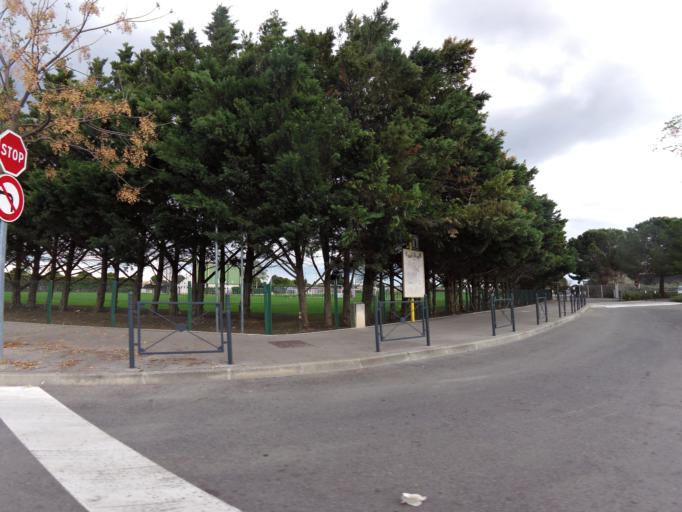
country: FR
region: Languedoc-Roussillon
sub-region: Departement de l'Herault
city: Lunel
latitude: 43.6889
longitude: 4.1347
